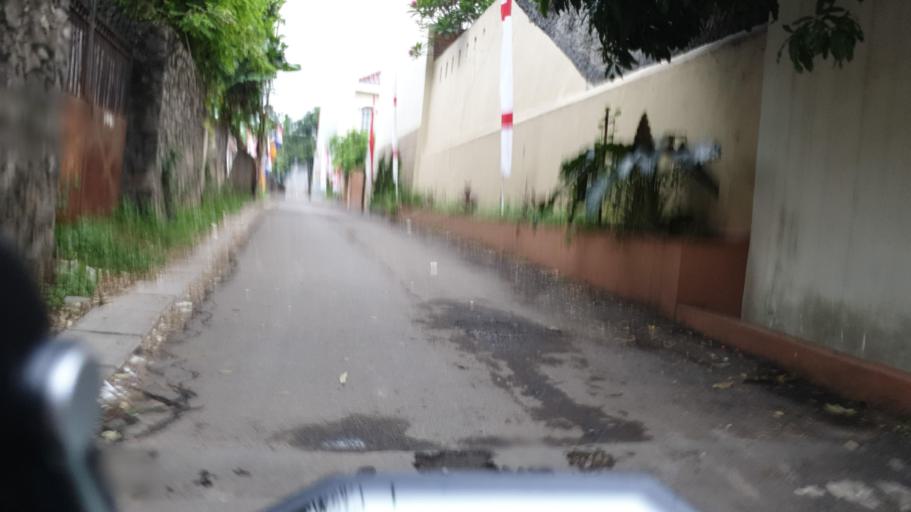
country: ID
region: West Java
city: Pamulang
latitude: -6.3245
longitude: 106.7693
